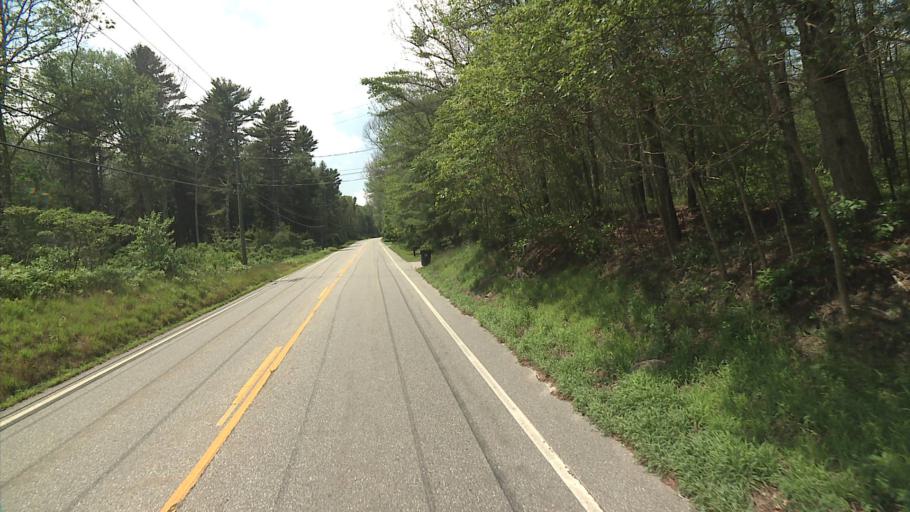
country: US
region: Rhode Island
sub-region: Washington County
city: Hopkinton
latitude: 41.5735
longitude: -71.8289
